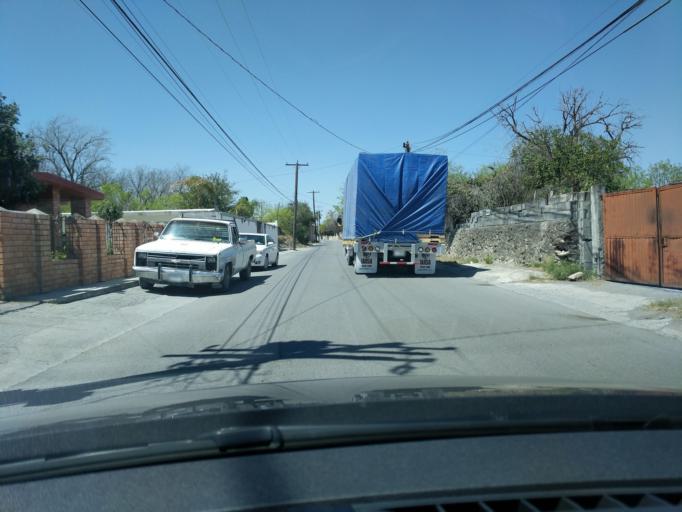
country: MX
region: Nuevo Leon
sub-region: Apodaca
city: Artemio Trevino
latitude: 25.8130
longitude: -100.1383
